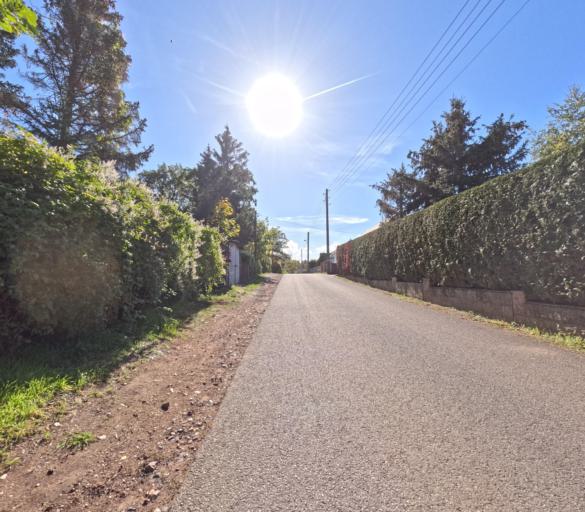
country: DE
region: Saxony
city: Radebeul
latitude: 51.1220
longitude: 13.6430
